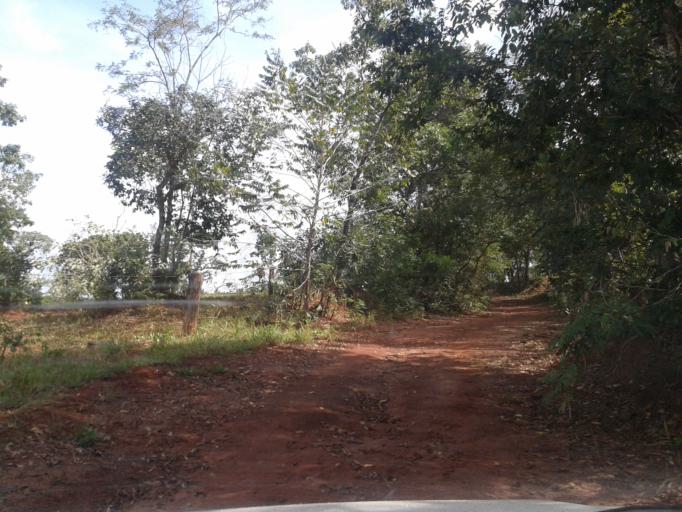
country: BR
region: Minas Gerais
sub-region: Campina Verde
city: Campina Verde
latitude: -19.4278
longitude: -49.6958
